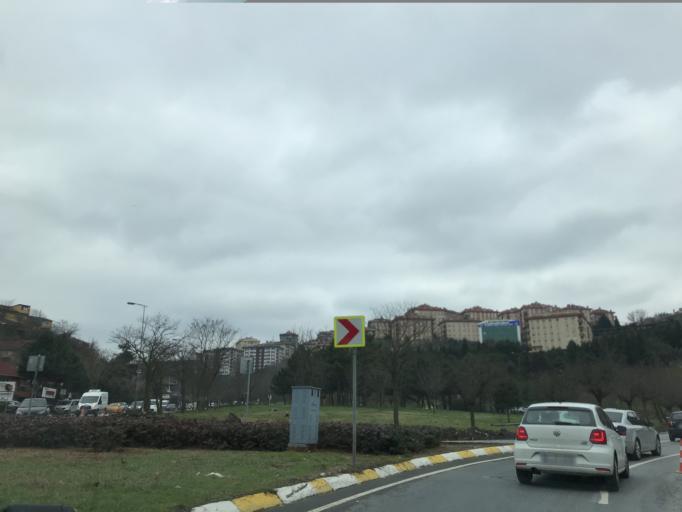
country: TR
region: Istanbul
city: Sisli
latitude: 41.1218
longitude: 29.0416
